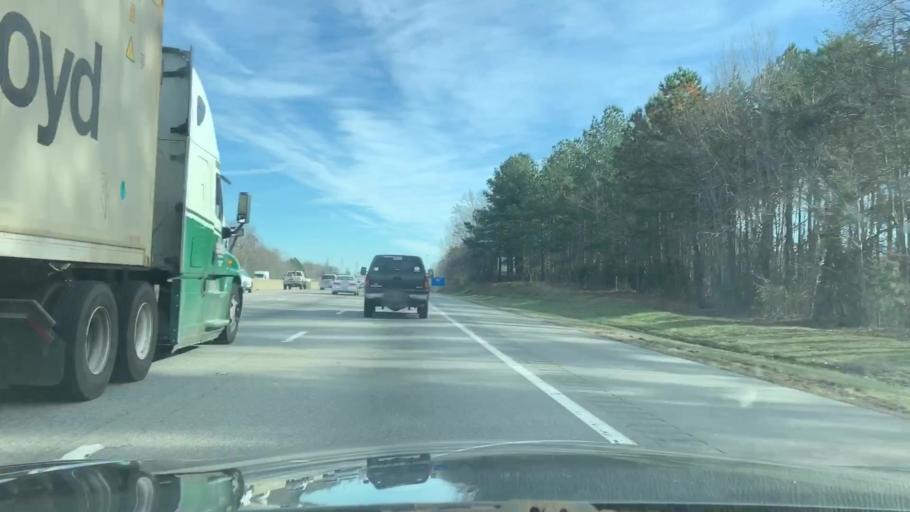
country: US
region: North Carolina
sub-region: Orange County
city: Hillsborough
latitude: 36.0738
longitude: -79.1796
